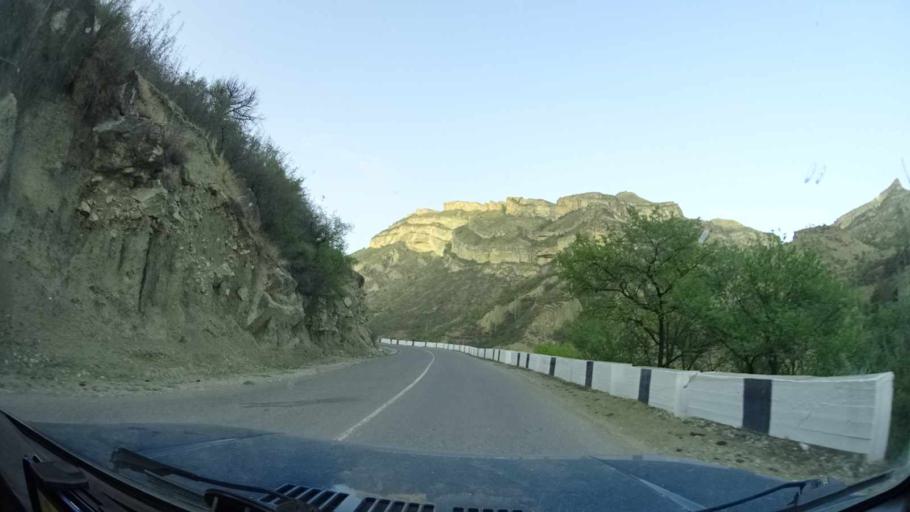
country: RU
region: Dagestan
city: Gunib
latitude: 42.3836
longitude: 46.9677
